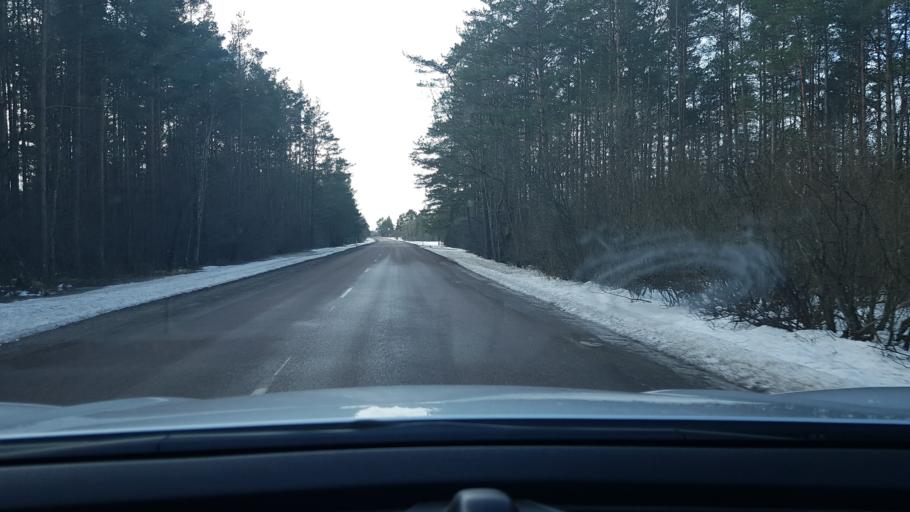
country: EE
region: Saare
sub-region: Kuressaare linn
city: Kuressaare
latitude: 58.3416
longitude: 22.5778
